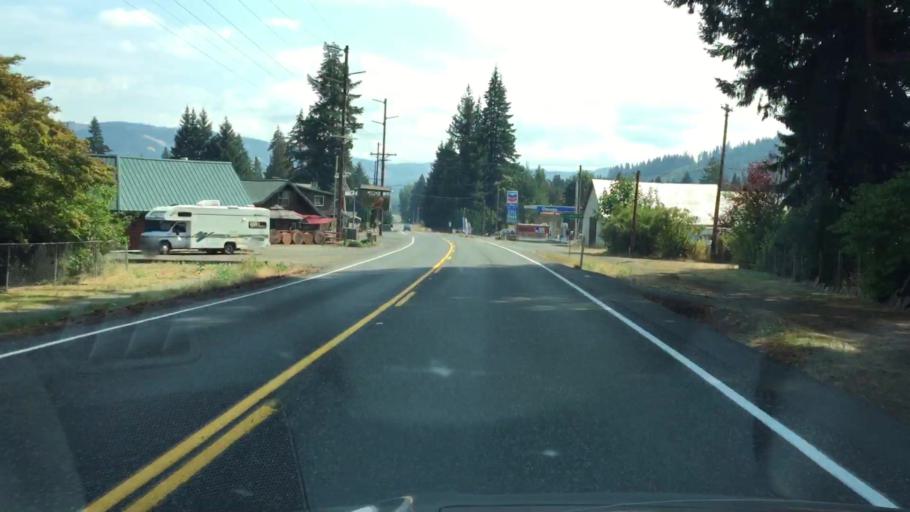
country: US
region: Washington
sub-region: Klickitat County
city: White Salmon
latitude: 45.8507
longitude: -121.5102
